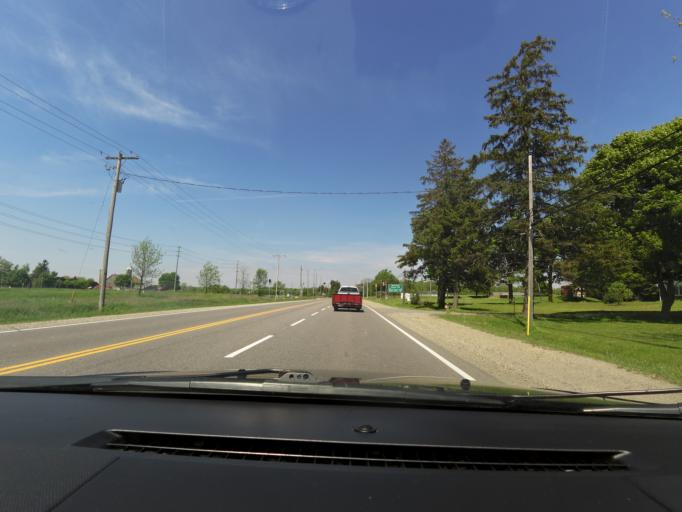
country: CA
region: Ontario
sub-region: Wellington County
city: Guelph
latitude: 43.5891
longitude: -80.1788
